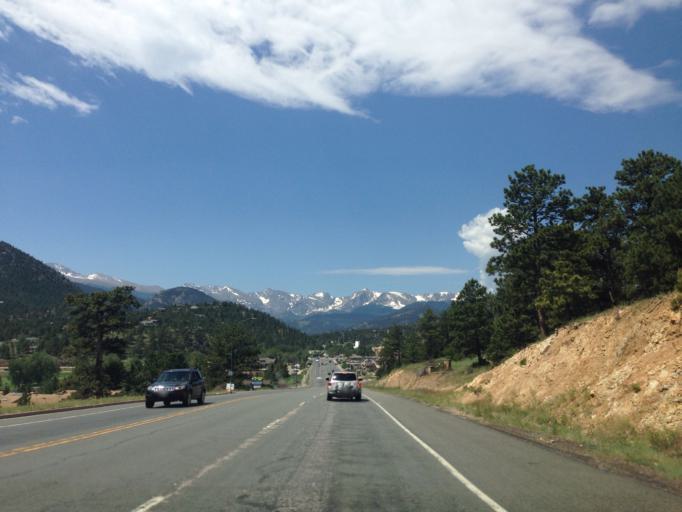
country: US
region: Colorado
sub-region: Larimer County
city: Estes Park
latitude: 40.3822
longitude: -105.5089
